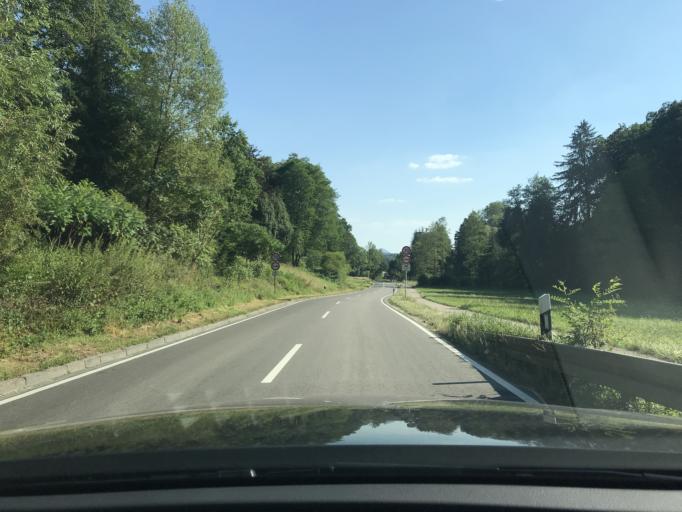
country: DE
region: Baden-Wuerttemberg
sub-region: Regierungsbezirk Stuttgart
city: Reichenbach an der Fils
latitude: 48.7212
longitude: 9.4639
